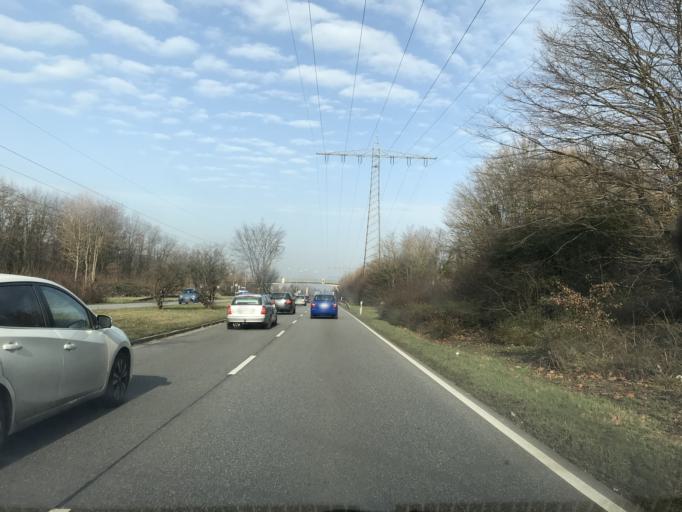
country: DE
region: Baden-Wuerttemberg
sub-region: Freiburg Region
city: Ebringen
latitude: 47.9983
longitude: 7.7992
